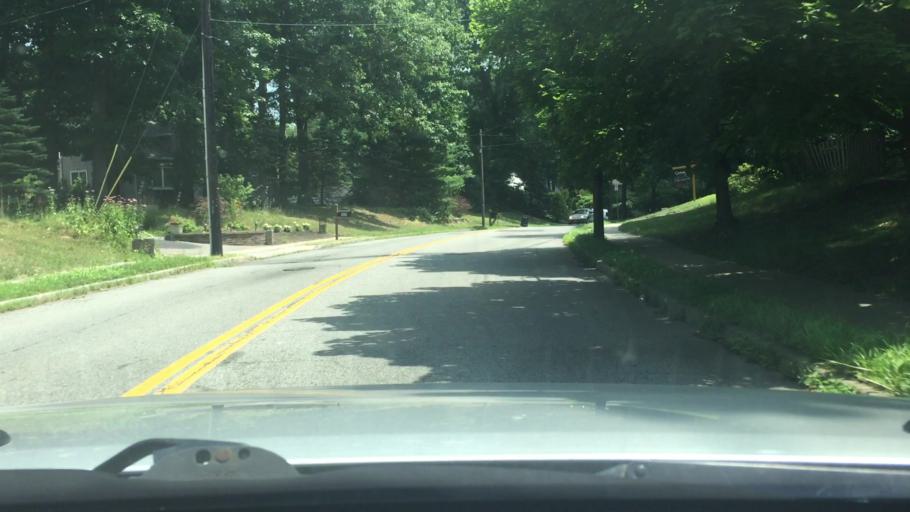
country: US
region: New Jersey
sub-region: Middlesex County
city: East Brunswick
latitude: 40.4136
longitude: -74.4096
